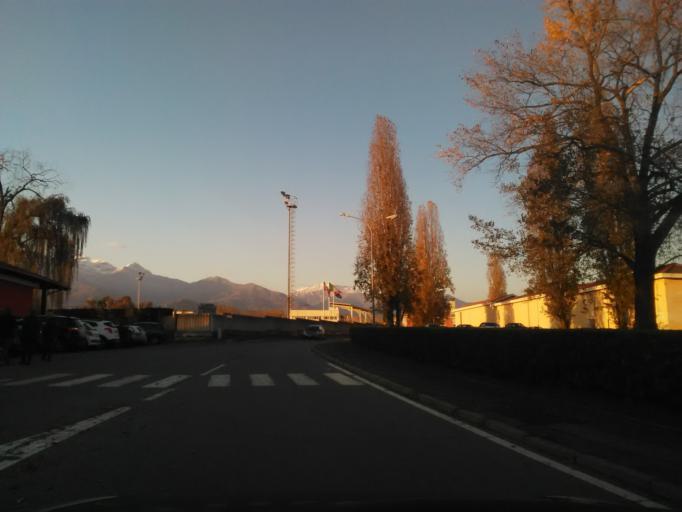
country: IT
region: Piedmont
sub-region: Provincia di Biella
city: Ponderano
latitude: 45.5363
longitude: 8.0497
